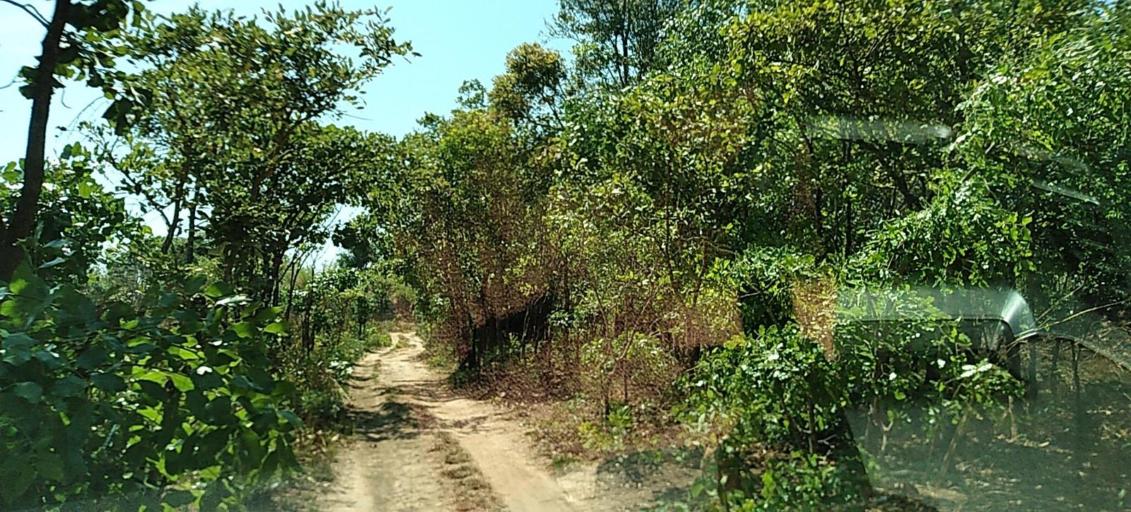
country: ZM
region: Copperbelt
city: Chililabombwe
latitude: -12.2895
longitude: 27.8914
